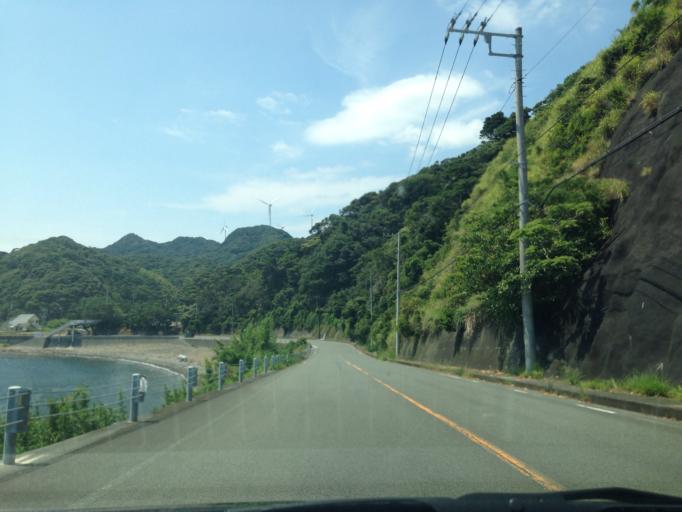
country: JP
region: Shizuoka
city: Shimoda
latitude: 34.6198
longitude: 138.8682
